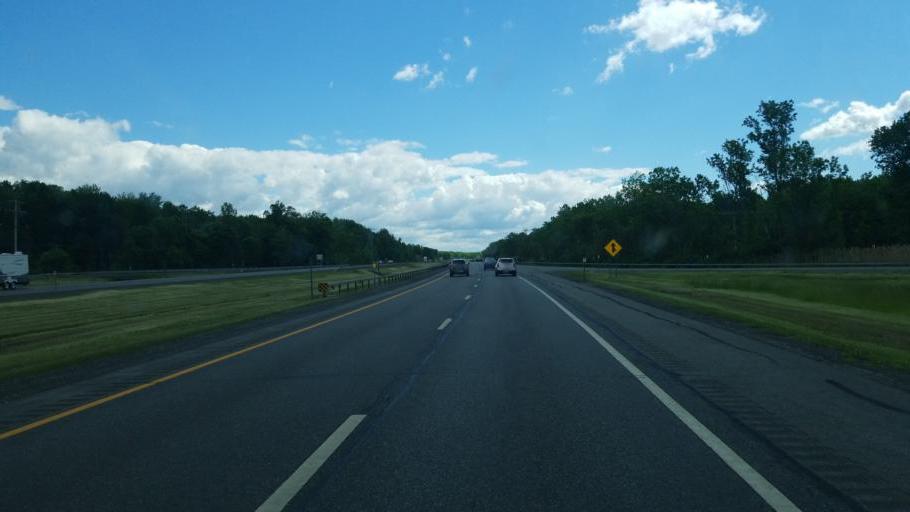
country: US
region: New York
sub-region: Madison County
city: Canastota
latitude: 43.0929
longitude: -75.7459
